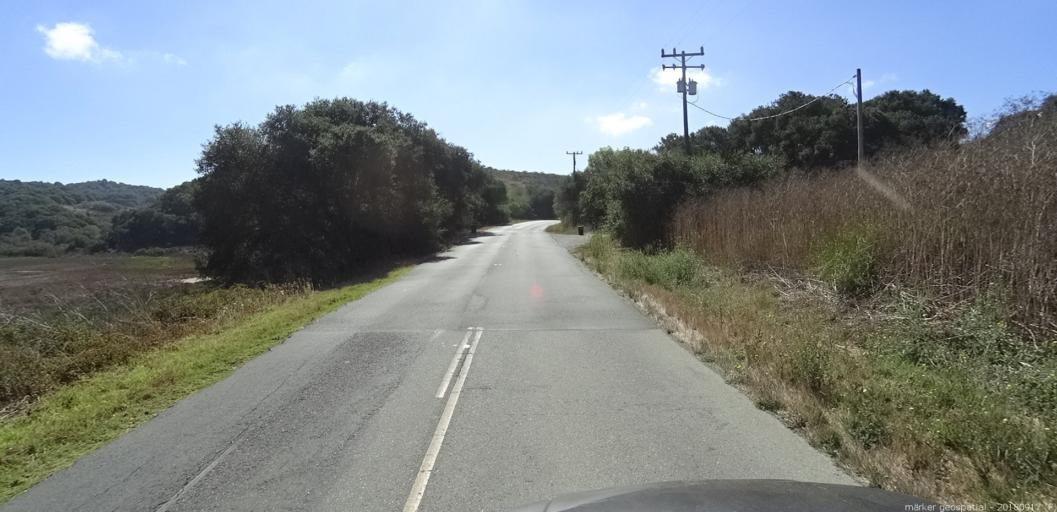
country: US
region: California
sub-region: Monterey County
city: Las Lomas
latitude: 36.8541
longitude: -121.7555
